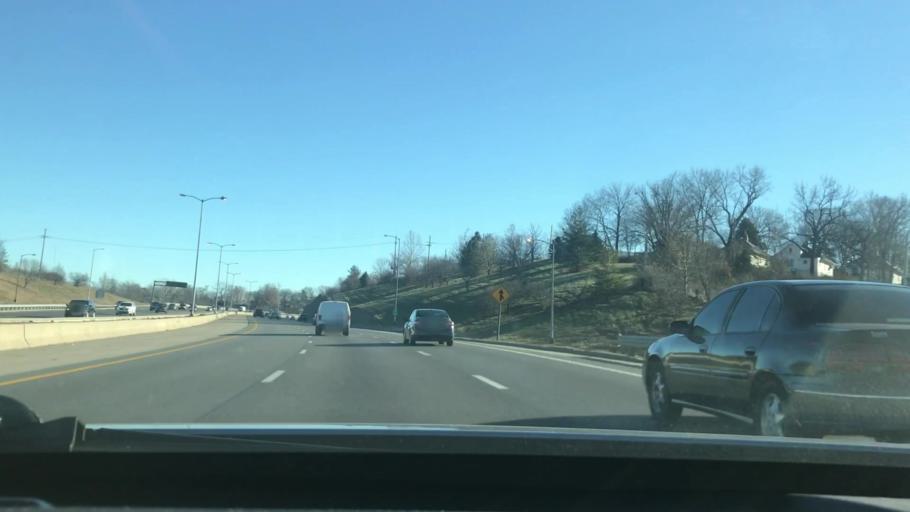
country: US
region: Kansas
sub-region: Johnson County
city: Westwood
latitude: 39.0392
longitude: -94.5581
